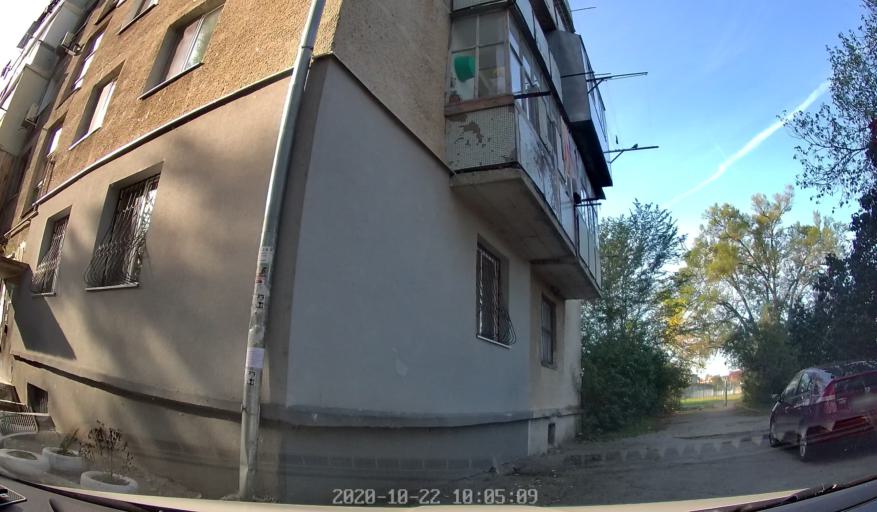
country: MD
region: Chisinau
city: Singera
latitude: 46.9403
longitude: 28.9247
